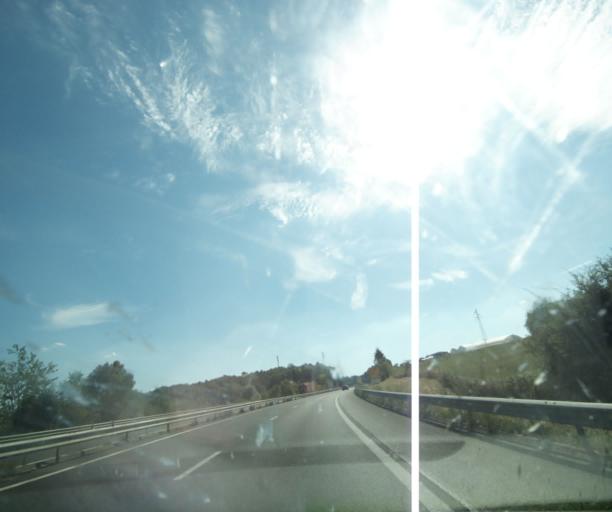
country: FR
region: Limousin
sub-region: Departement de la Correze
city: Brive-la-Gaillarde
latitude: 45.1188
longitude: 1.5014
